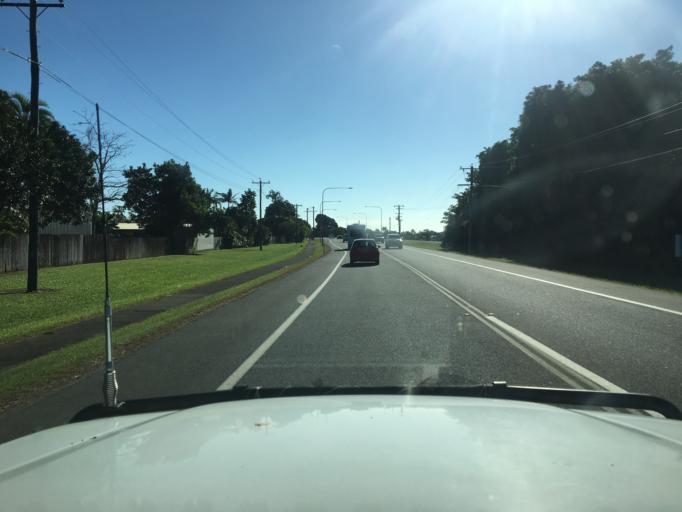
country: AU
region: Queensland
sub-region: Cairns
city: Redlynch
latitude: -16.8642
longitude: 145.6918
